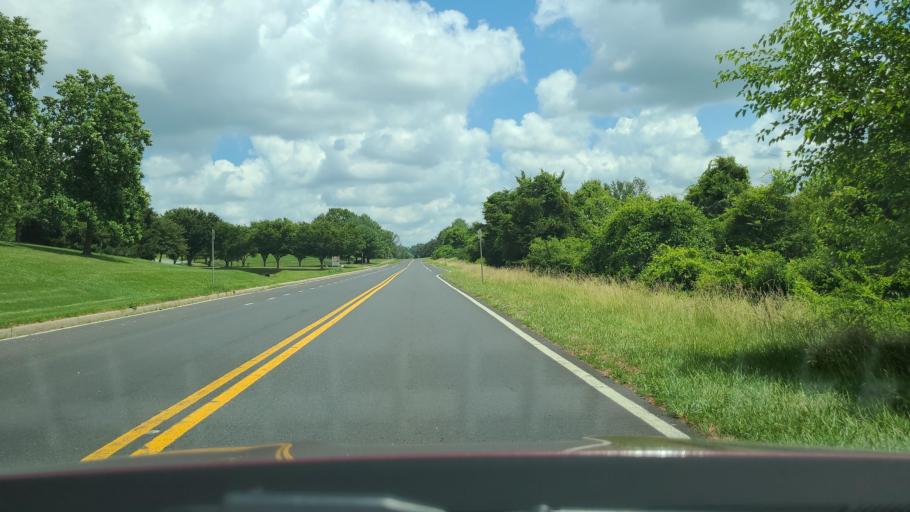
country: US
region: Maryland
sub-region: Carroll County
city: Westminster
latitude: 39.5427
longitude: -77.0042
